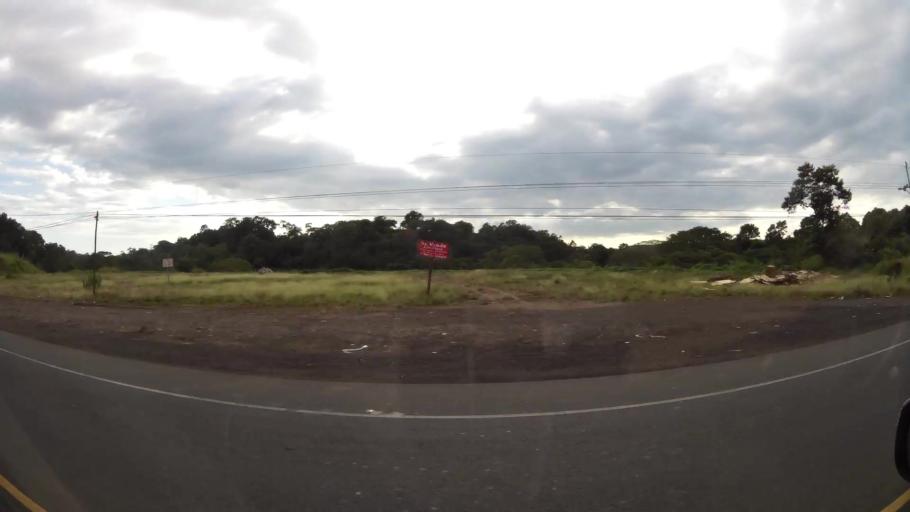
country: CR
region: Puntarenas
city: Esparza
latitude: 9.9045
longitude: -84.6606
